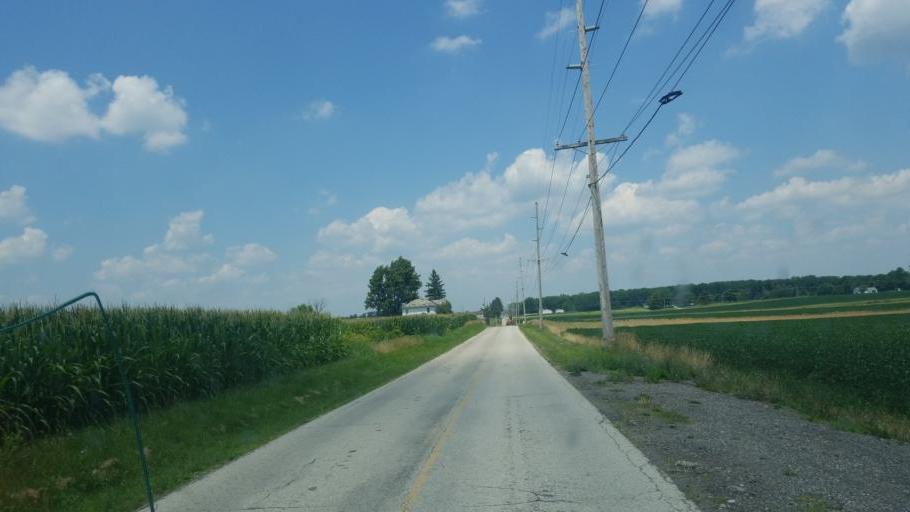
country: US
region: Ohio
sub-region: Richland County
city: Shelby
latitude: 40.8517
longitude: -82.6773
